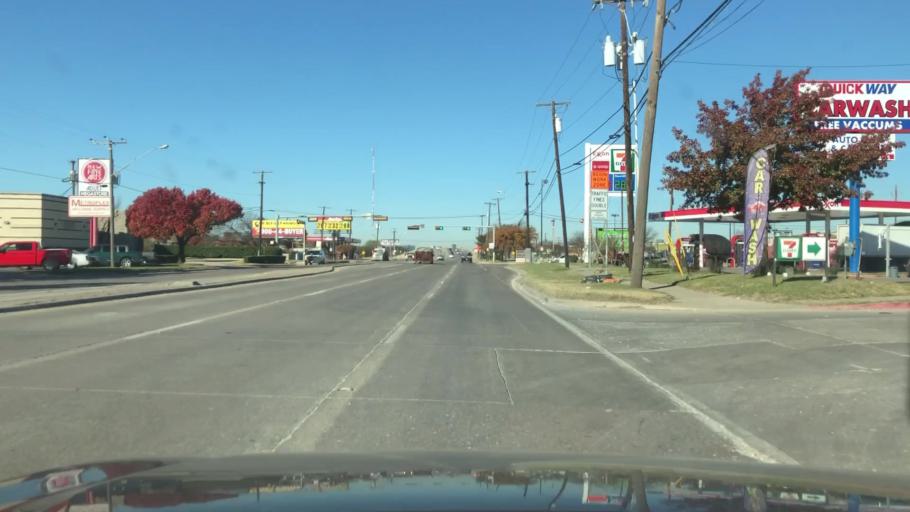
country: US
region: Texas
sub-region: Dallas County
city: Farmers Branch
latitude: 32.8678
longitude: -96.9096
